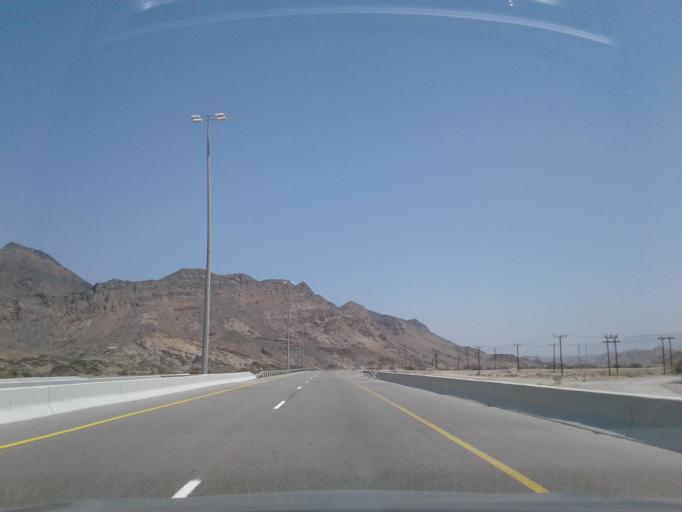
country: OM
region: Muhafazat Masqat
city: Muscat
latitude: 23.3025
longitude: 58.7356
